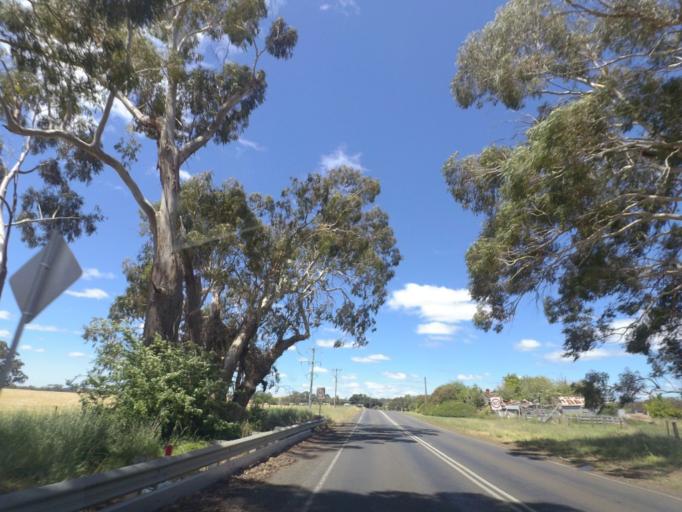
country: AU
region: Victoria
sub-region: Mount Alexander
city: Castlemaine
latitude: -37.3308
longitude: 144.1790
